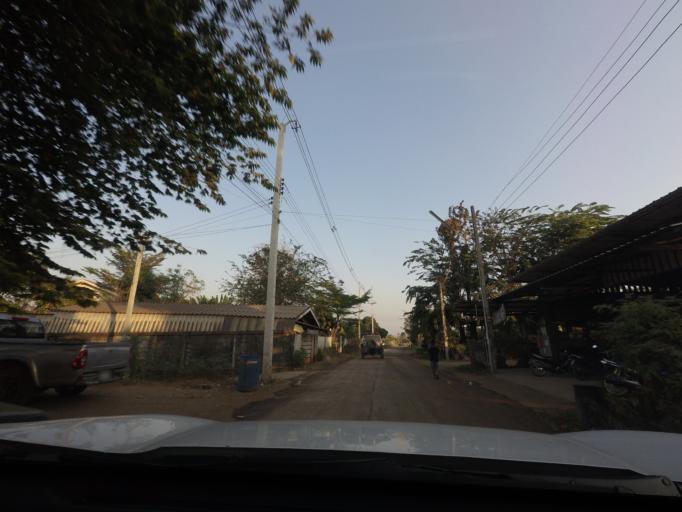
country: TH
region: Nakhon Ratchasima
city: Pak Chong
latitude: 14.6456
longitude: 101.4012
